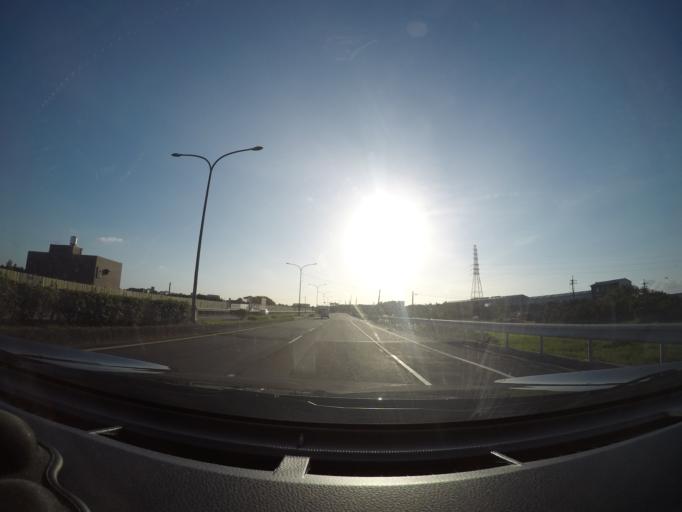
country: TW
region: Taiwan
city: Taoyuan City
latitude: 25.0741
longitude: 121.2012
